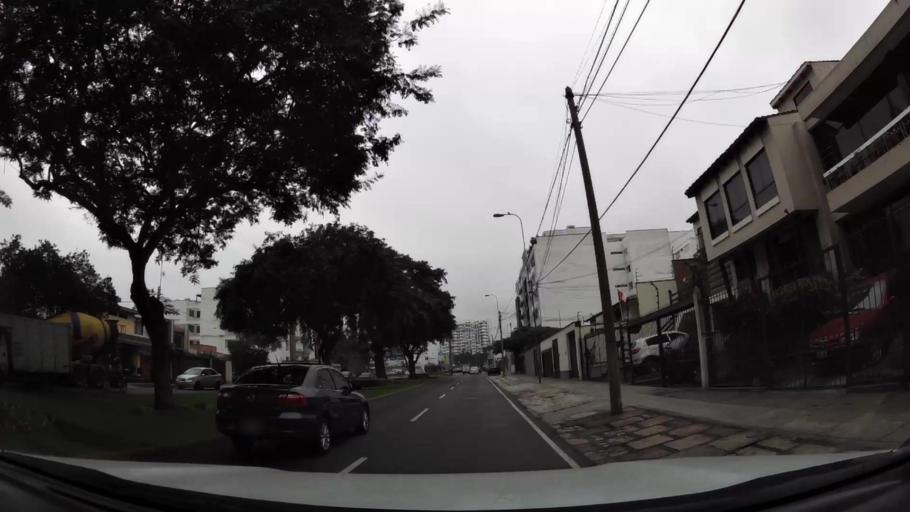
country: PE
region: Lima
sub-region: Lima
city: Surco
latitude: -12.1184
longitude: -77.0096
